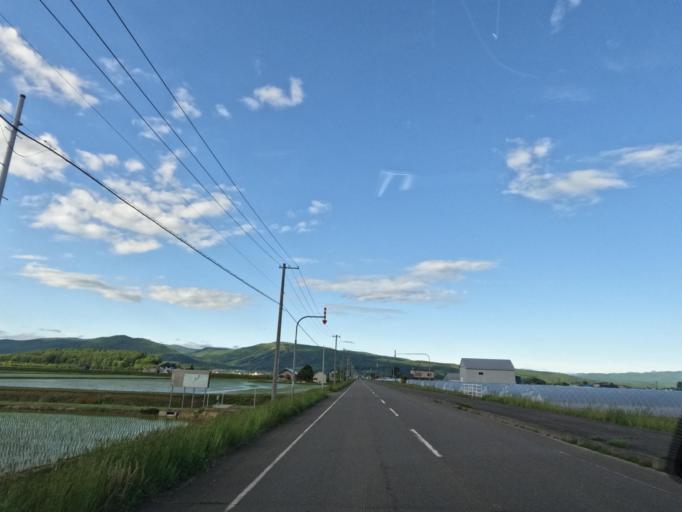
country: JP
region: Hokkaido
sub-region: Asahikawa-shi
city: Asahikawa
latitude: 43.8907
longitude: 142.4664
